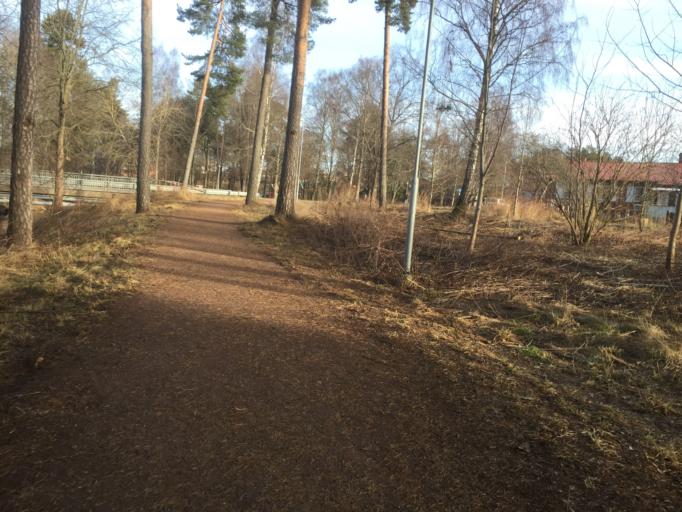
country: SE
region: Joenkoeping
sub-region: Aneby Kommun
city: Aneby
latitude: 57.8349
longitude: 14.8131
